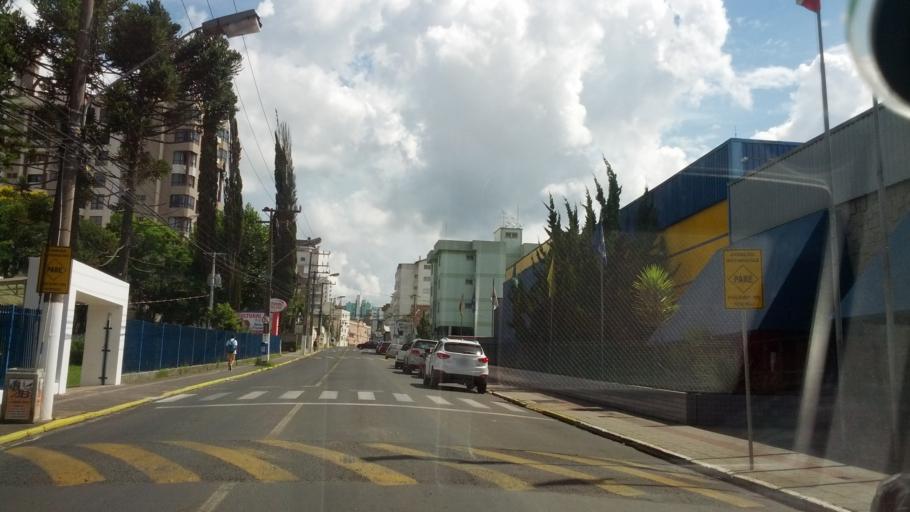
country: BR
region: Santa Catarina
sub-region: Lages
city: Lages
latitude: -27.8130
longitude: -50.3210
